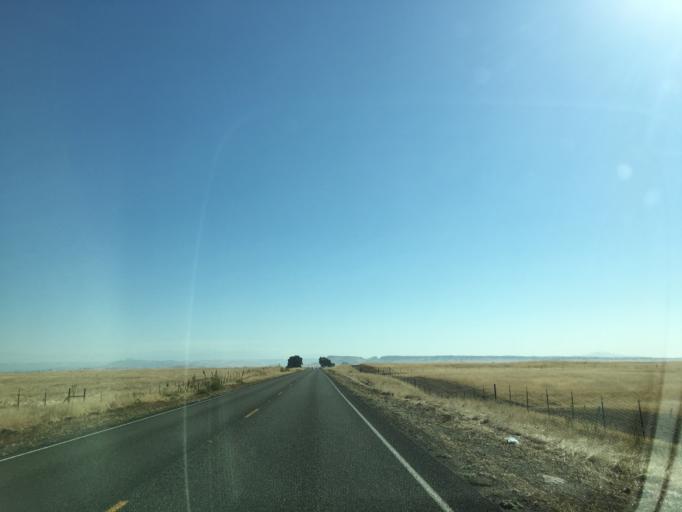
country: US
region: California
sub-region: Madera County
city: Bonadelle Ranchos-Madera Ranchos
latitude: 37.0103
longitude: -119.8504
